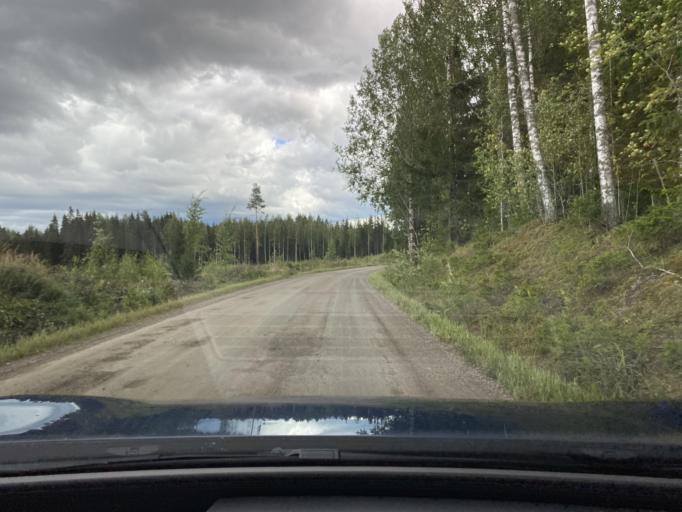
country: FI
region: Pirkanmaa
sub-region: Lounais-Pirkanmaa
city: Punkalaidun
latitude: 61.2249
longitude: 23.1581
